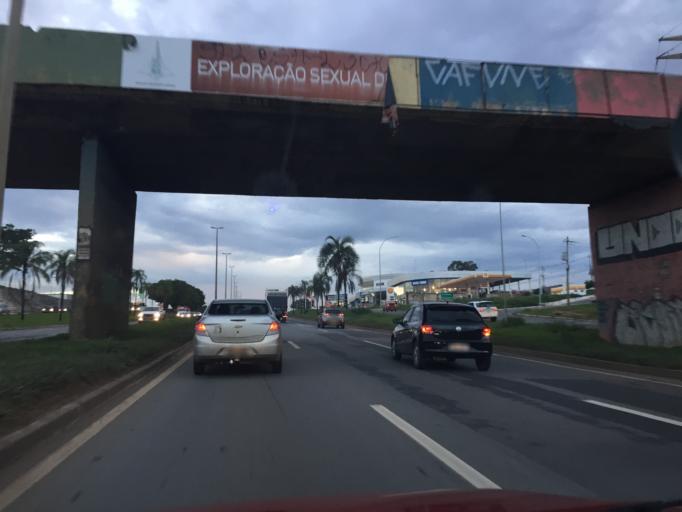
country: BR
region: Federal District
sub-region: Brasilia
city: Brasilia
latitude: -15.8473
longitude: -47.9544
